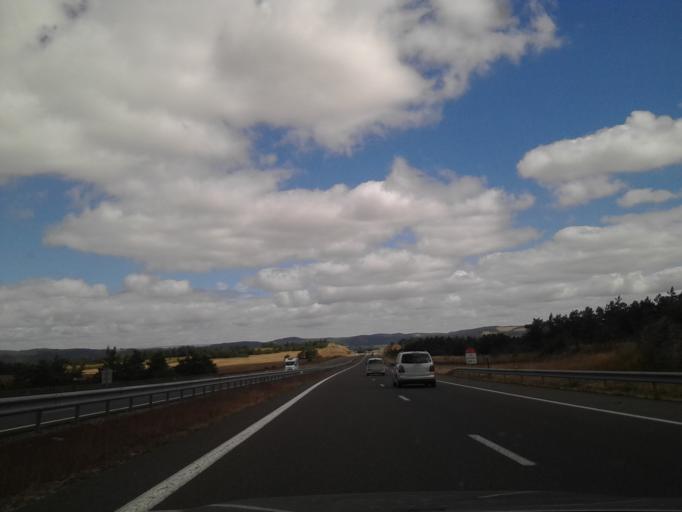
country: FR
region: Midi-Pyrenees
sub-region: Departement de l'Aveyron
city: Severac-le-Chateau
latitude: 44.2904
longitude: 3.0953
